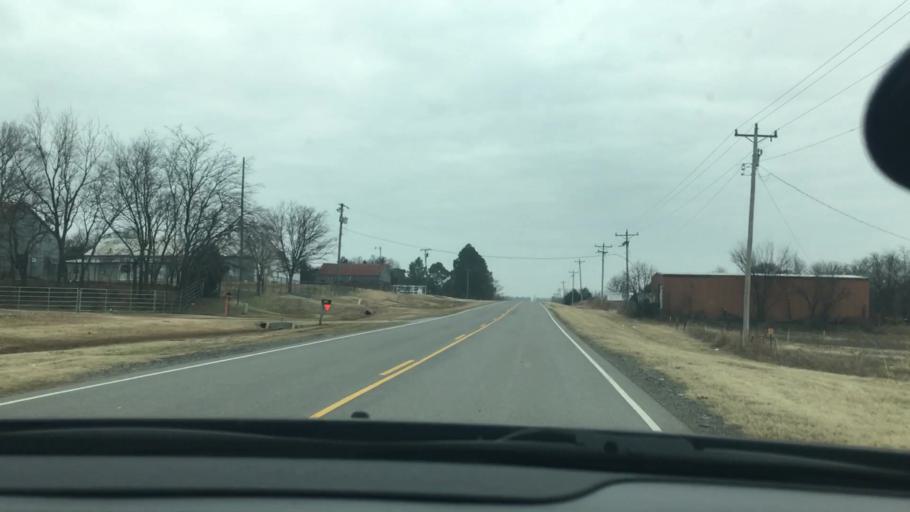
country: US
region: Oklahoma
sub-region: Carter County
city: Healdton
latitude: 34.2541
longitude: -97.4923
